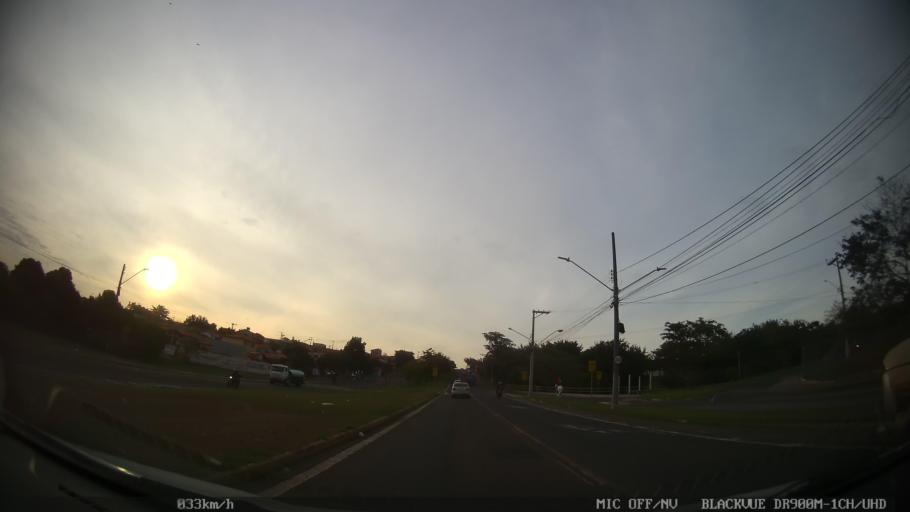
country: BR
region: Sao Paulo
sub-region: Limeira
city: Limeira
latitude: -22.5817
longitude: -47.3759
